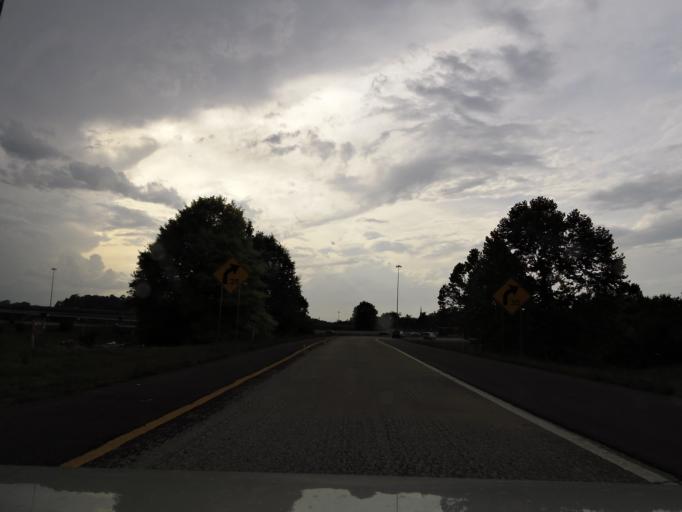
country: US
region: Tennessee
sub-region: Knox County
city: Knoxville
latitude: 35.9995
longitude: -83.9557
